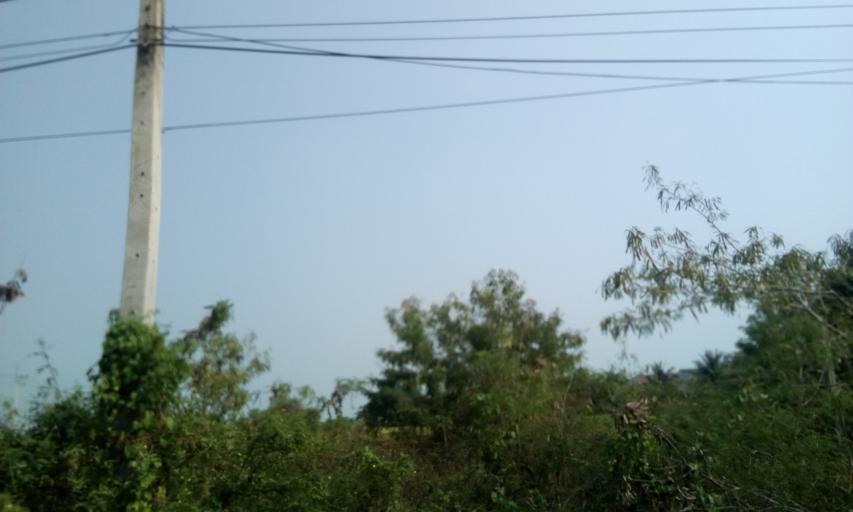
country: TH
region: Pathum Thani
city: Ban Lam Luk Ka
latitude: 13.9766
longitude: 100.7527
